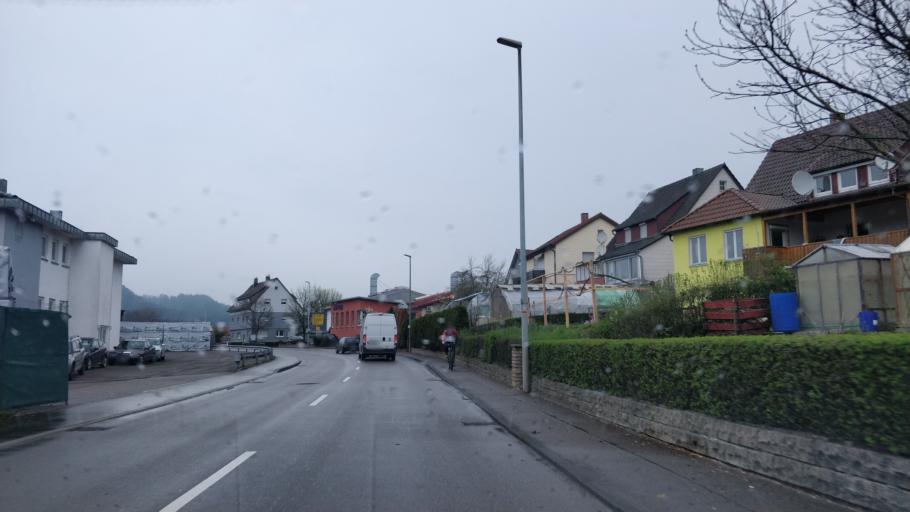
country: DE
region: Baden-Wuerttemberg
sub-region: Regierungsbezirk Stuttgart
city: Oberrot
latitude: 49.0140
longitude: 9.6712
